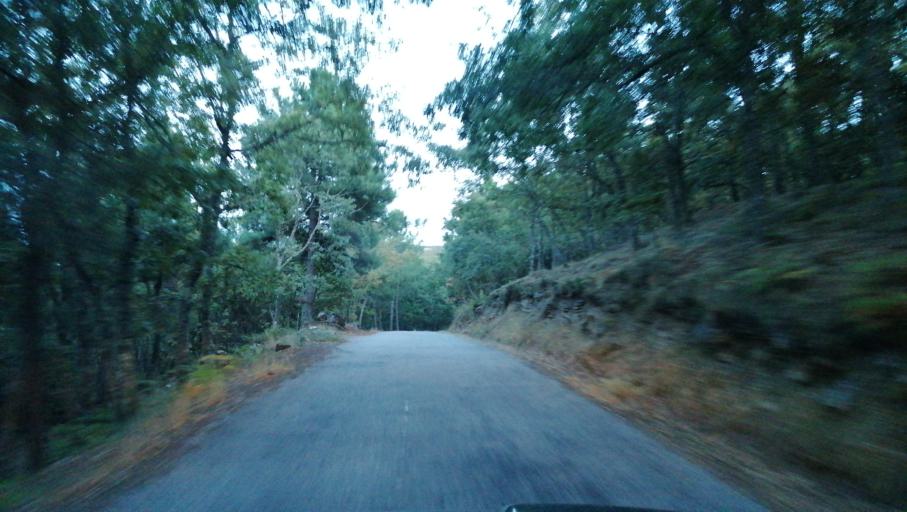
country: PT
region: Vila Real
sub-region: Vila Pouca de Aguiar
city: Vila Pouca de Aguiar
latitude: 41.5573
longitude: -7.6573
